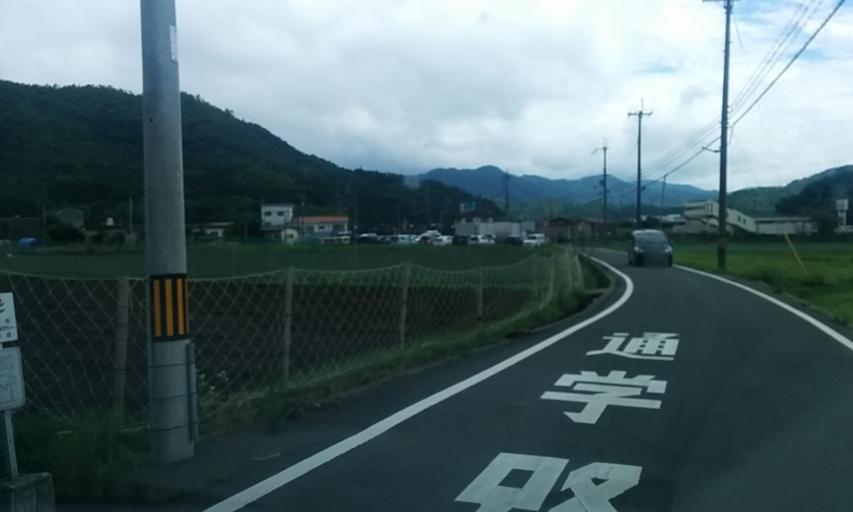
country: JP
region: Kyoto
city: Kameoka
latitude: 35.0916
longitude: 135.4963
